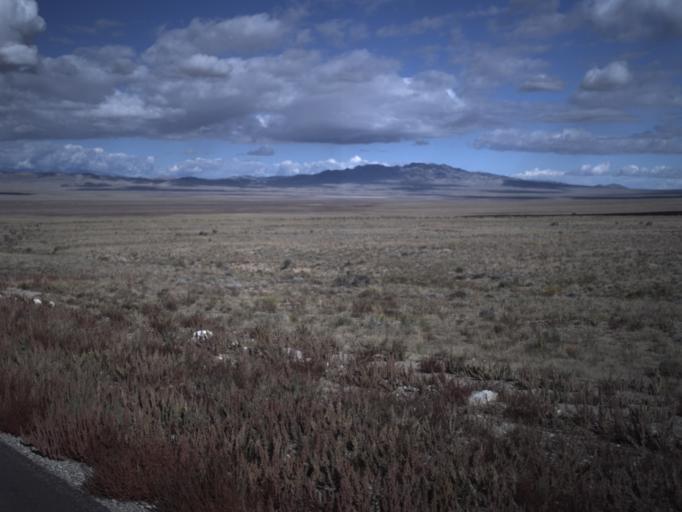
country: US
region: Utah
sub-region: Beaver County
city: Milford
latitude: 38.5069
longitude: -113.6130
